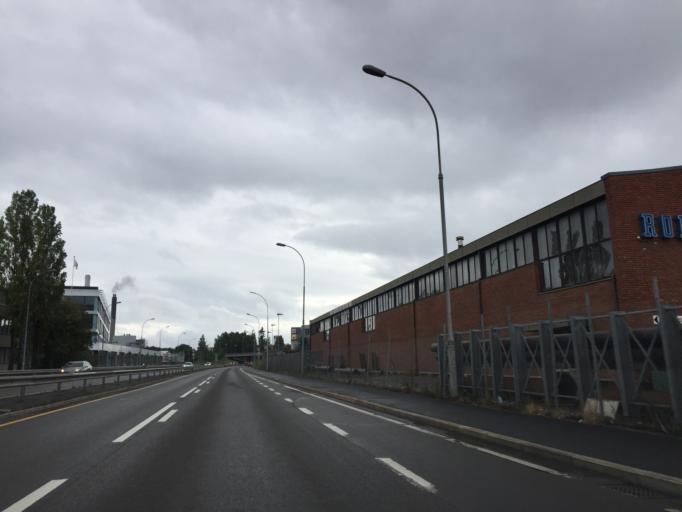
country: NO
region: Oslo
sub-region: Oslo
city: Oslo
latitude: 59.9357
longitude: 10.8324
